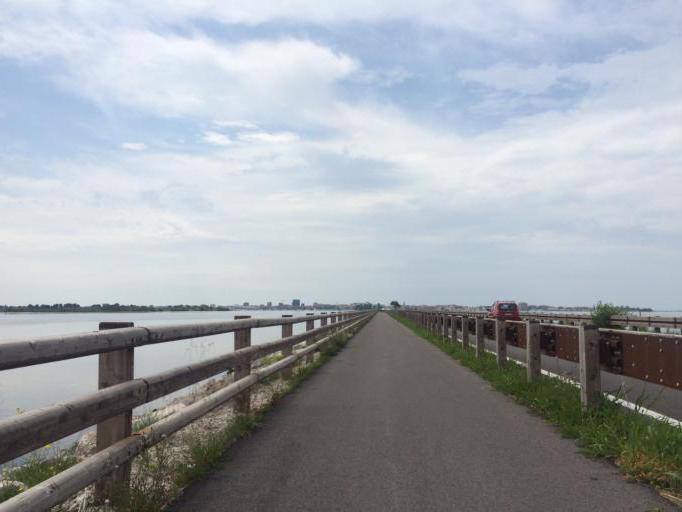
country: IT
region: Friuli Venezia Giulia
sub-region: Provincia di Gorizia
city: Grado
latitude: 45.7012
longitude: 13.3832
